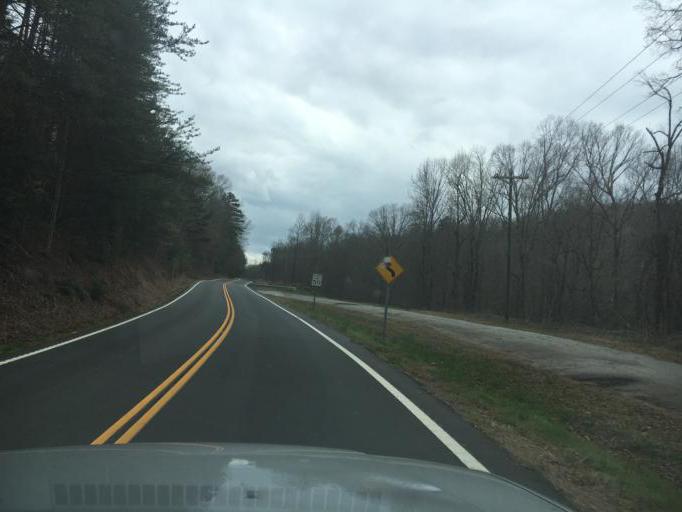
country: US
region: South Carolina
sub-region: Pickens County
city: Pickens
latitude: 34.9868
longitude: -82.7544
